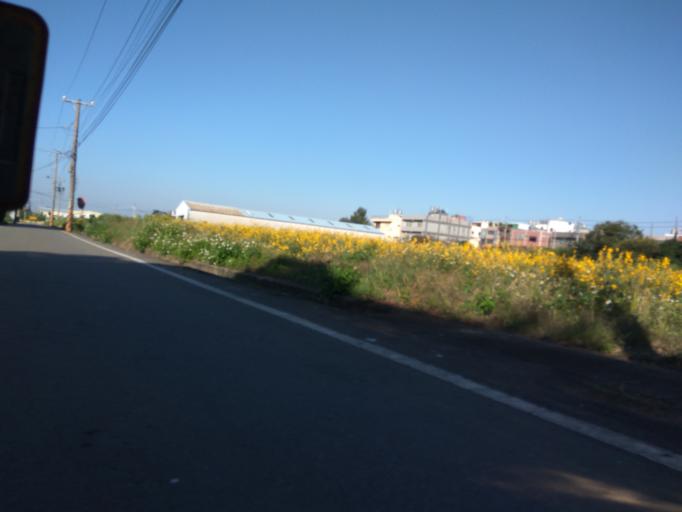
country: TW
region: Taiwan
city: Taoyuan City
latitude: 25.0081
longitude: 121.2264
